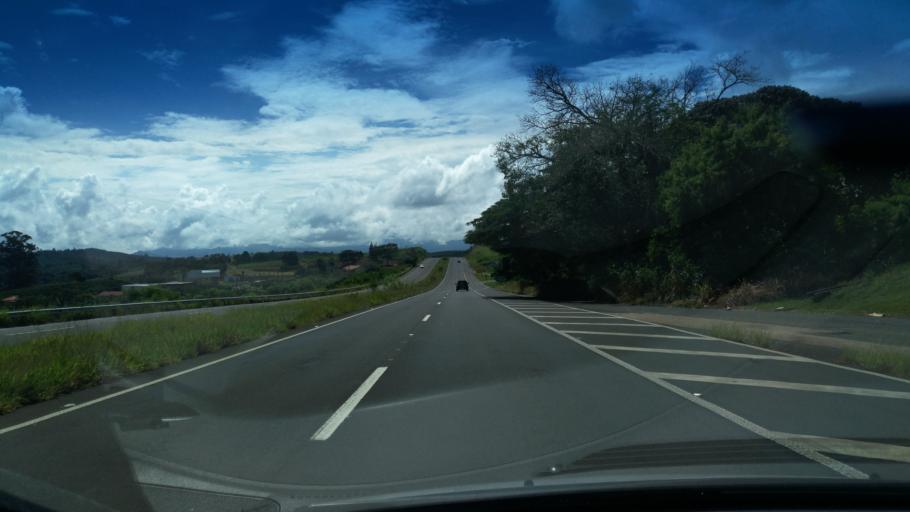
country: BR
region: Sao Paulo
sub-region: Santo Antonio Do Jardim
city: Espirito Santo do Pinhal
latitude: -22.1740
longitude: -46.7468
